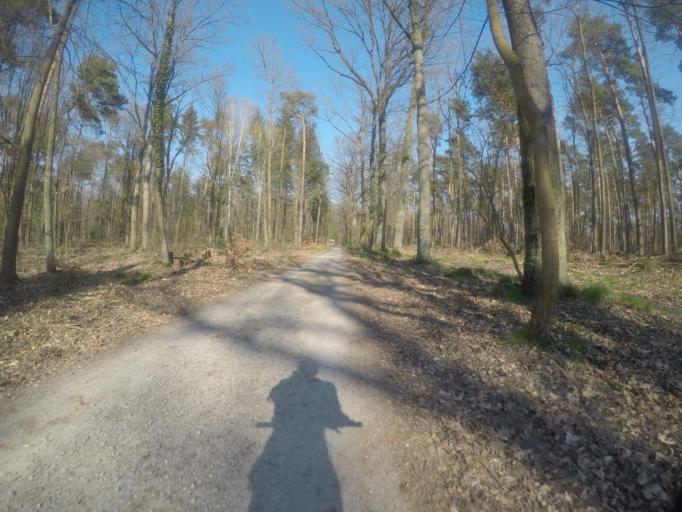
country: DE
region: Berlin
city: Wannsee
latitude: 52.4105
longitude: 13.1826
